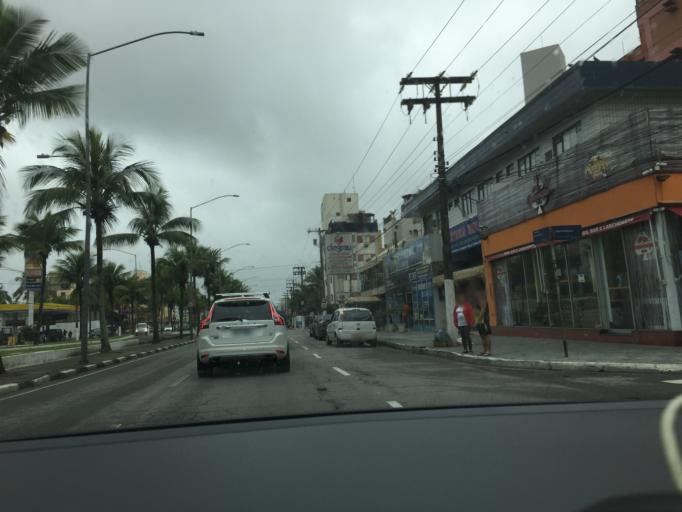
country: BR
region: Sao Paulo
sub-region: Guaruja
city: Guaruja
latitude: -23.9829
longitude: -46.2337
